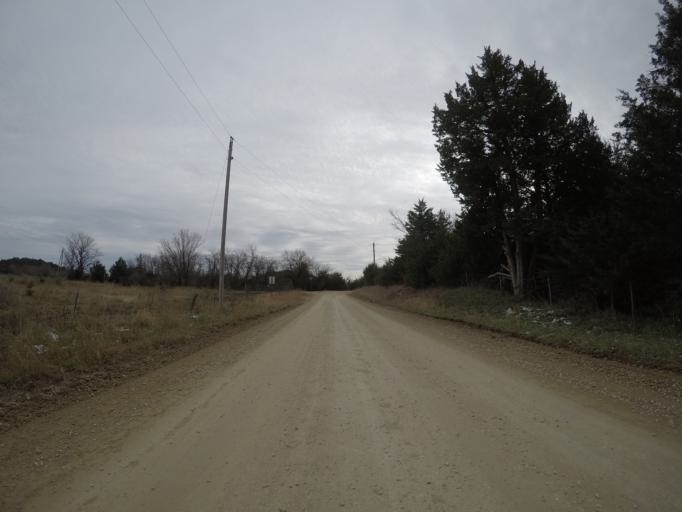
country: US
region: Kansas
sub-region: Riley County
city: Ogden
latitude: 39.1754
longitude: -96.6782
